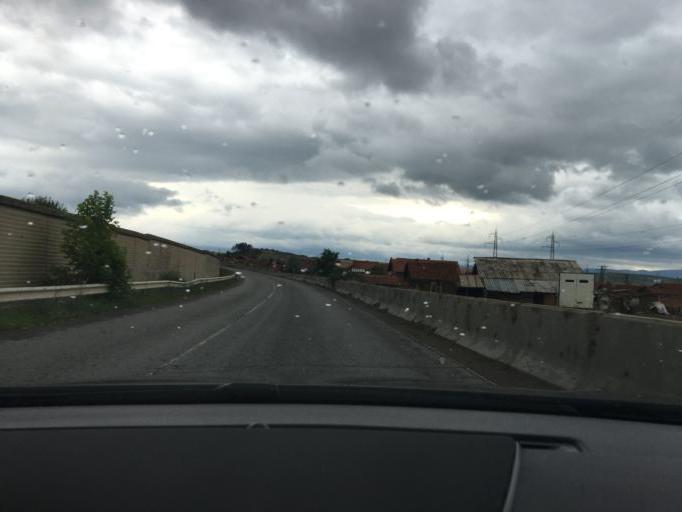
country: BG
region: Kyustendil
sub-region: Obshtina Kyustendil
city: Kyustendil
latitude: 42.2973
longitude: 22.7178
